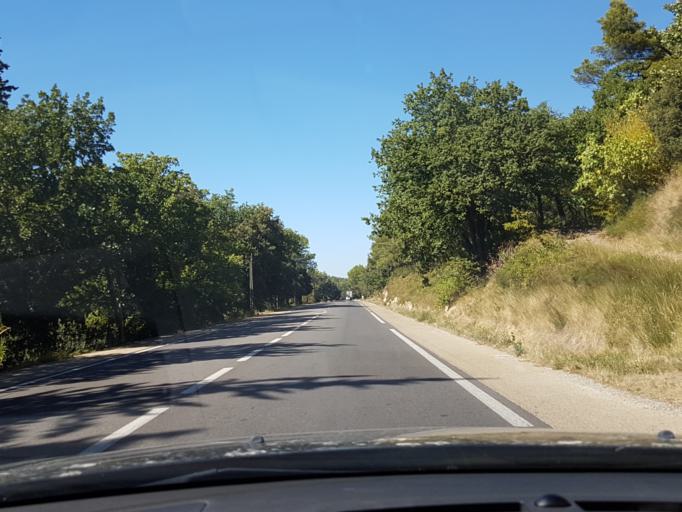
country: FR
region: Provence-Alpes-Cote d'Azur
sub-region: Departement des Bouches-du-Rhone
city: Orgon
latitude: 43.7969
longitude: 5.0288
